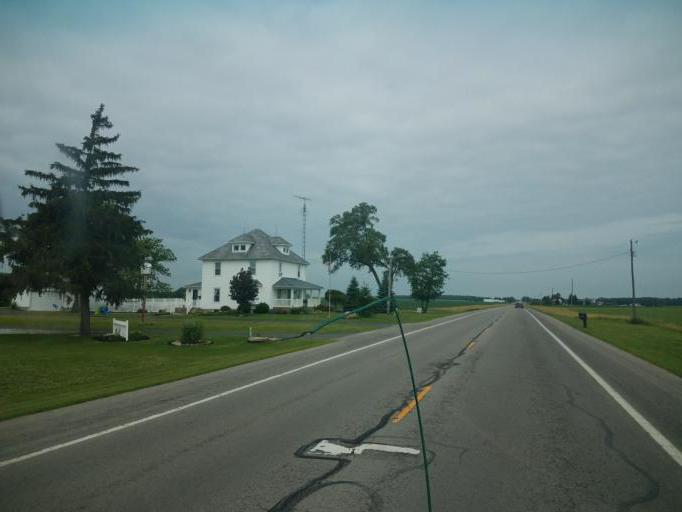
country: US
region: Ohio
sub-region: Hardin County
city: Kenton
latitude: 40.6717
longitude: -83.6626
